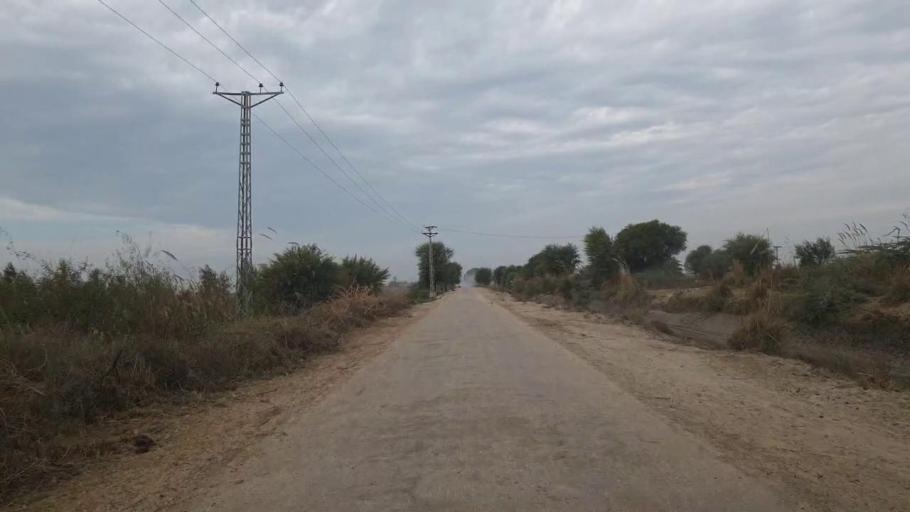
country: PK
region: Sindh
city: Jhol
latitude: 25.9912
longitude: 68.8949
